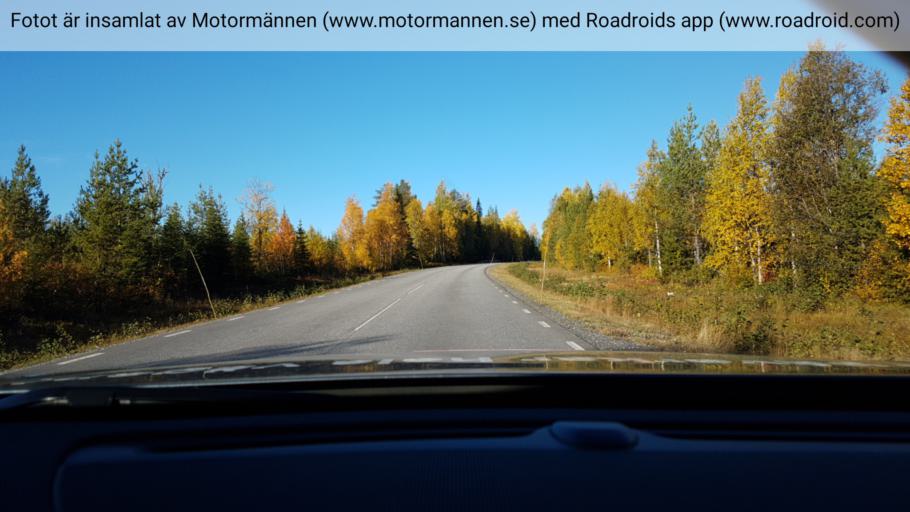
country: SE
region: Vaesterbotten
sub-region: Skelleftea Kommun
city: Storvik
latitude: 65.3380
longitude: 20.5389
